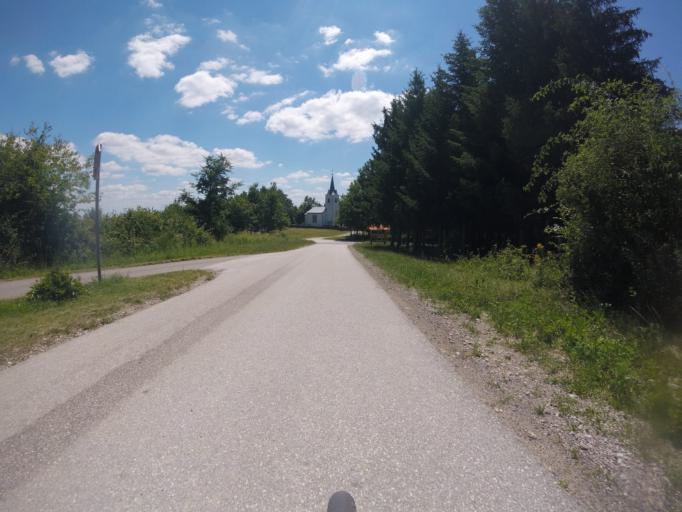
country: SI
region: Metlika
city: Metlika
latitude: 45.6968
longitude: 15.3869
